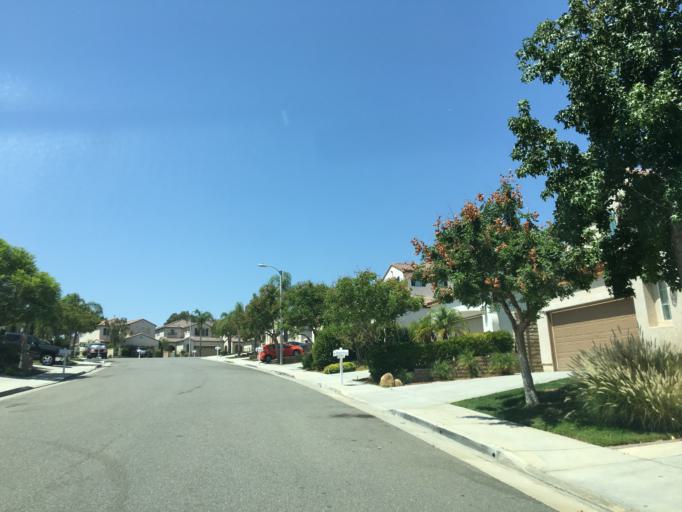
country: US
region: California
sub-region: Los Angeles County
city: Castaic
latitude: 34.5018
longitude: -118.6194
